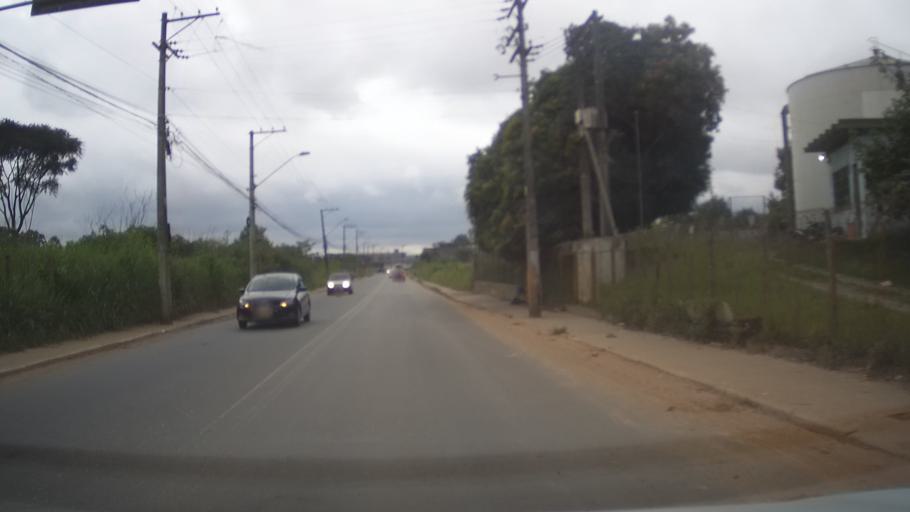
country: BR
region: Sao Paulo
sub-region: Guarulhos
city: Guarulhos
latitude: -23.4080
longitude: -46.4418
